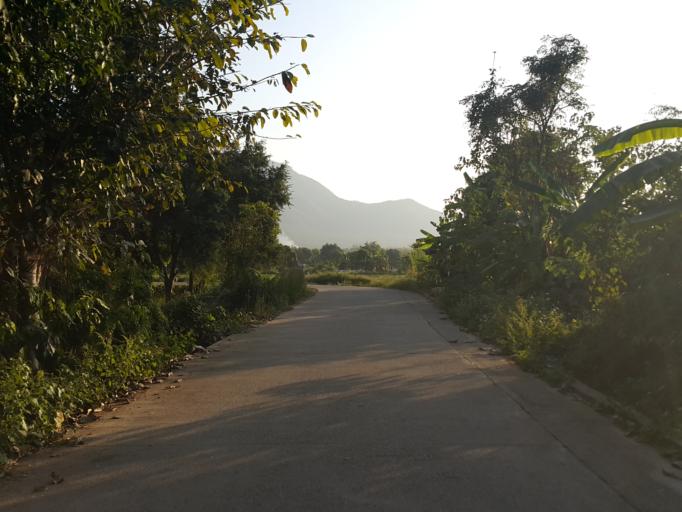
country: TH
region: Chiang Mai
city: Mae On
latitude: 18.7589
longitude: 99.2570
